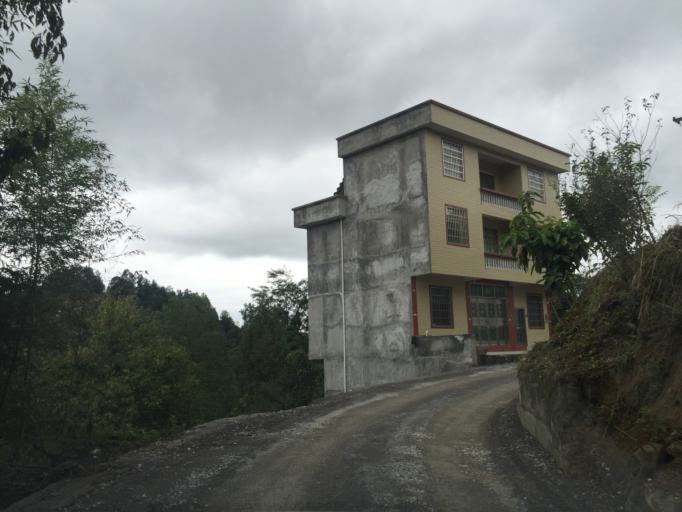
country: CN
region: Guizhou Sheng
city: Shiqian
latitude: 27.6816
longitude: 108.1142
